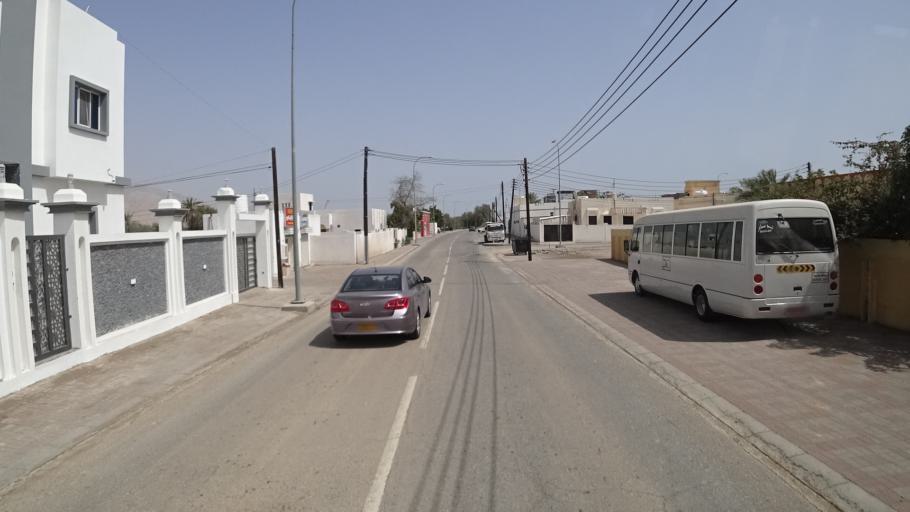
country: OM
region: Muhafazat Masqat
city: Muscat
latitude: 23.2386
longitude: 58.9107
